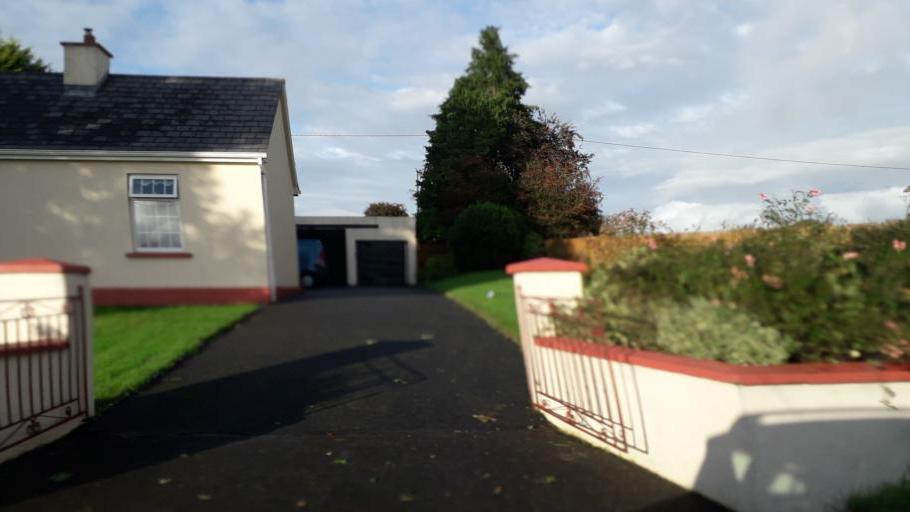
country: IE
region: Connaught
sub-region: Roscommon
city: Roscommon
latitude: 53.7735
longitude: -8.2343
